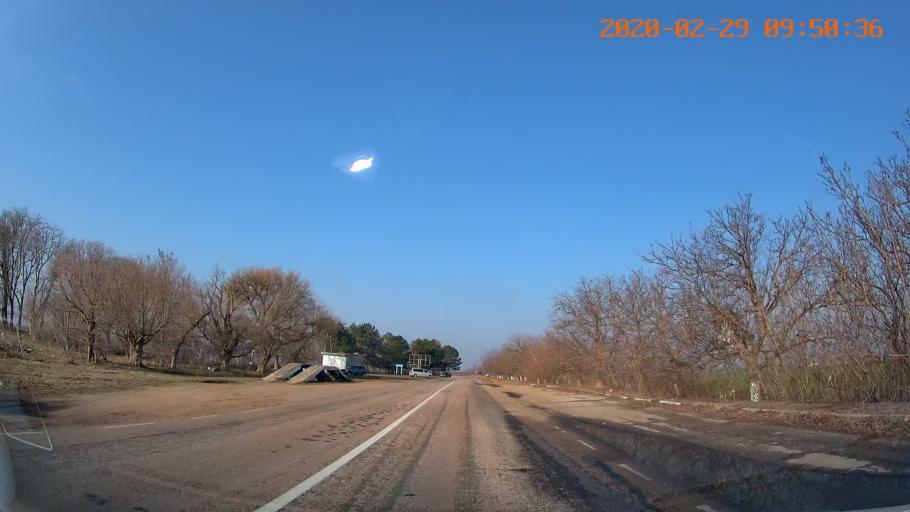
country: MD
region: Telenesti
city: Slobozia
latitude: 46.7027
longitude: 29.7528
